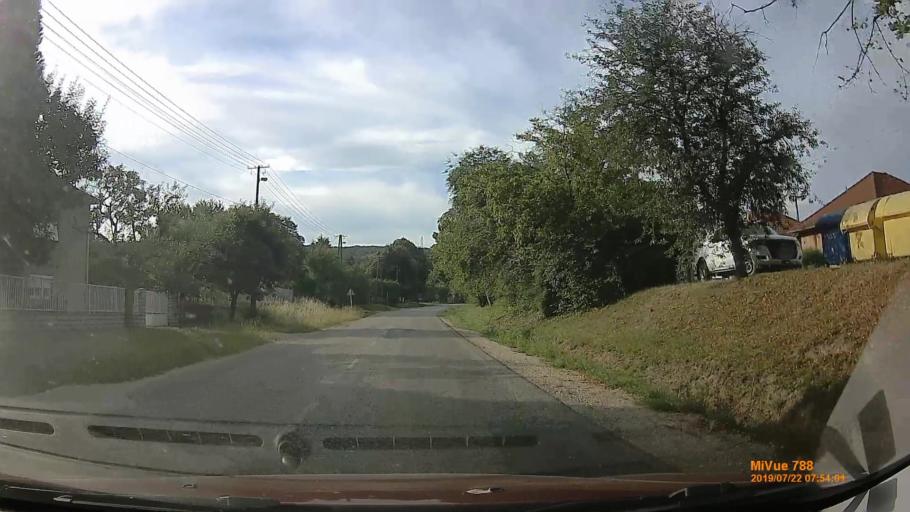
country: HU
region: Veszprem
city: Ajka
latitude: 47.0443
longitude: 17.5563
